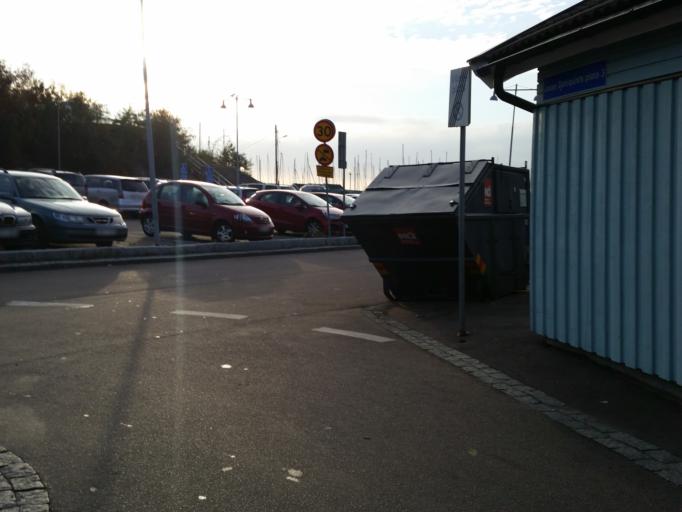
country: SE
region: Vaestra Goetaland
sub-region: Goteborg
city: Styrso
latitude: 57.6612
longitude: 11.8424
